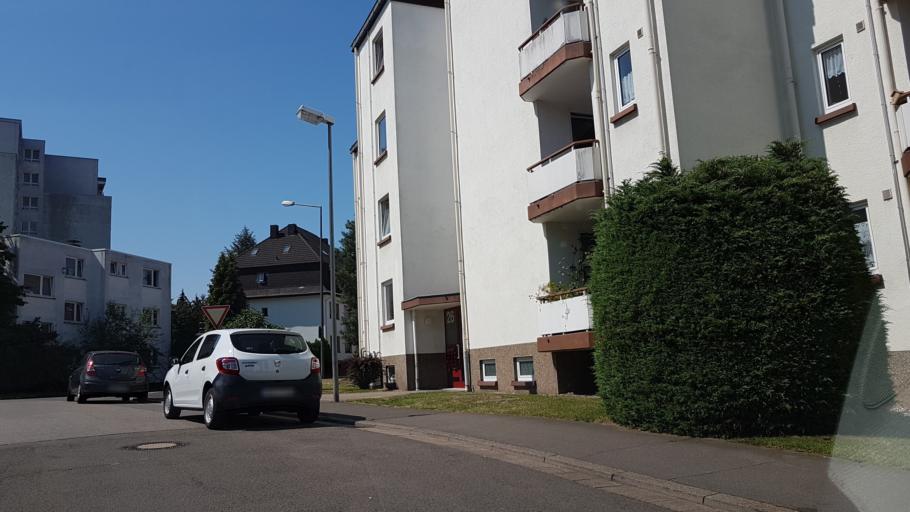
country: DE
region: Saarland
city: Homburg
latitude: 49.3136
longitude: 7.3330
